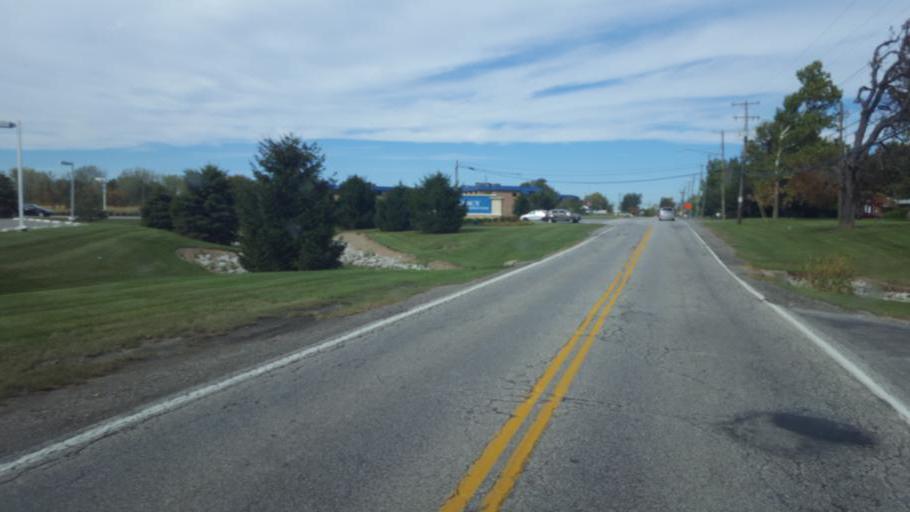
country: US
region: Ohio
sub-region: Lorain County
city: Amherst
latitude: 41.4375
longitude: -82.2353
